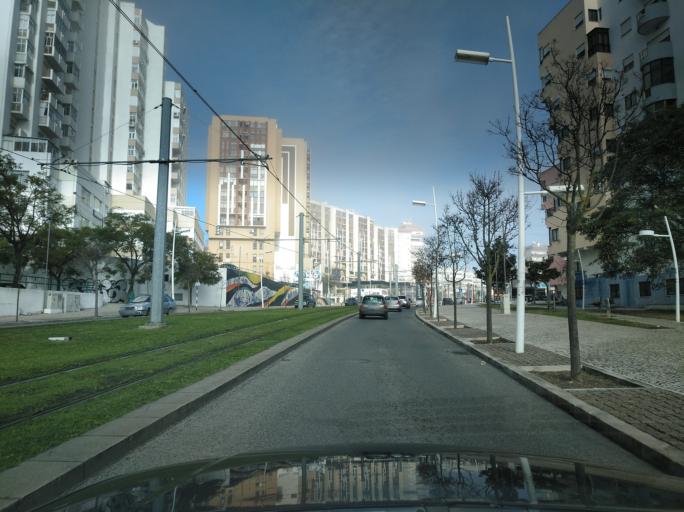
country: PT
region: Setubal
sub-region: Almada
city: Pragal
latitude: 38.6736
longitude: -9.1665
